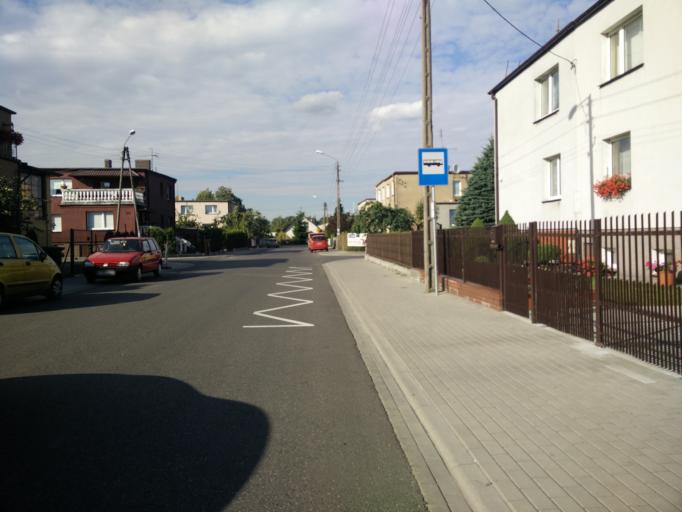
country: PL
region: Greater Poland Voivodeship
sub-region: Powiat sredzki
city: Sroda Wielkopolska
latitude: 52.2349
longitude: 17.2552
